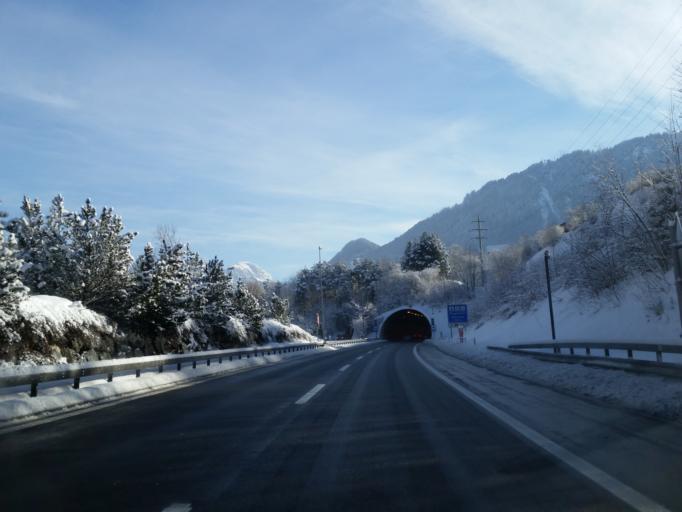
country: CH
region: Saint Gallen
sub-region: Wahlkreis Sarganserland
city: Quarten
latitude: 47.1103
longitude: 9.2339
